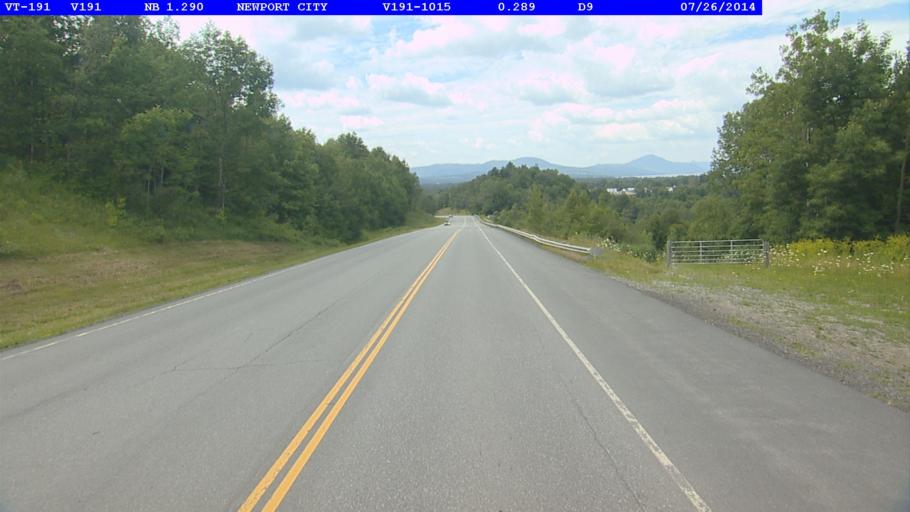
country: US
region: Vermont
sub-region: Orleans County
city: Newport
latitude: 44.9351
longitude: -72.1864
